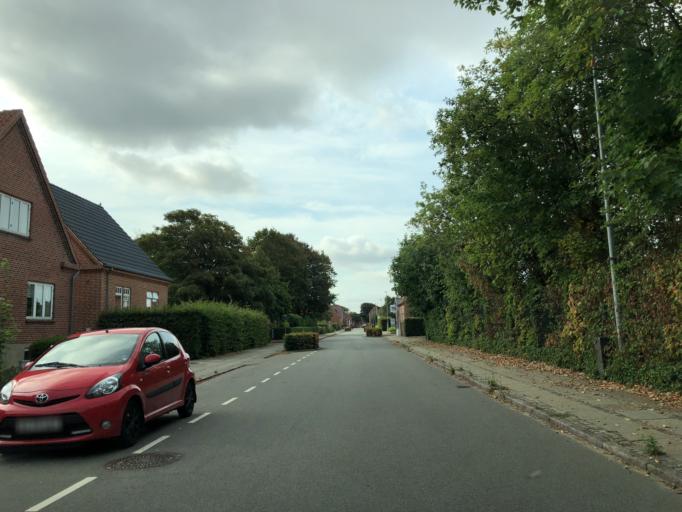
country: DK
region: Central Jutland
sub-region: Ringkobing-Skjern Kommune
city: Skjern
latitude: 55.9521
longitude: 8.4928
